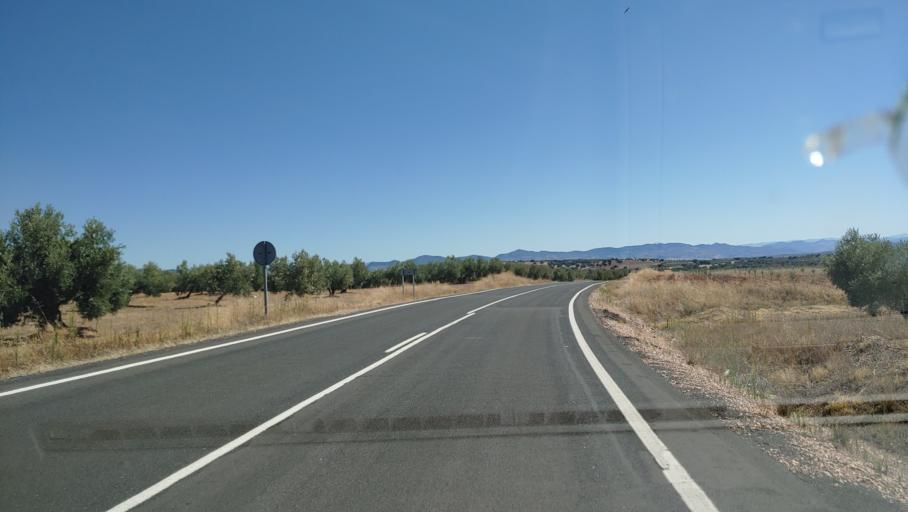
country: ES
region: Castille-La Mancha
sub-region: Provincia de Ciudad Real
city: Albaladejo
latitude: 38.5714
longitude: -2.7846
